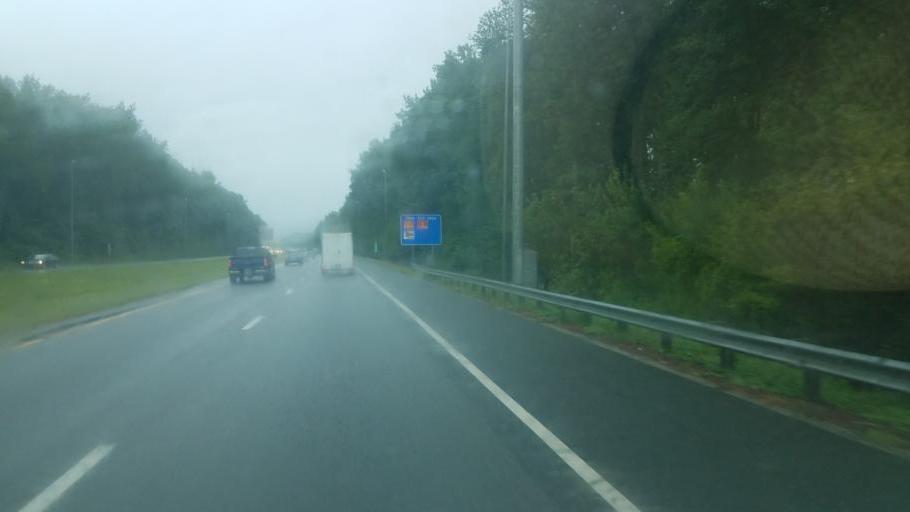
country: US
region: Virginia
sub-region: City of Chesapeake
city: Chesapeake
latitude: 36.7597
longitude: -76.3199
